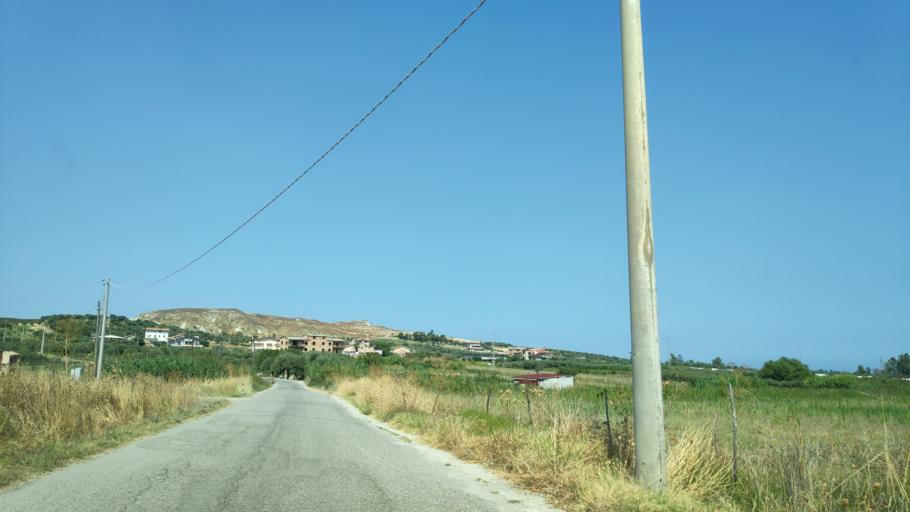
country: IT
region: Calabria
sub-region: Provincia di Reggio Calabria
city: Monasterace Marina
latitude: 38.4238
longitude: 16.5428
